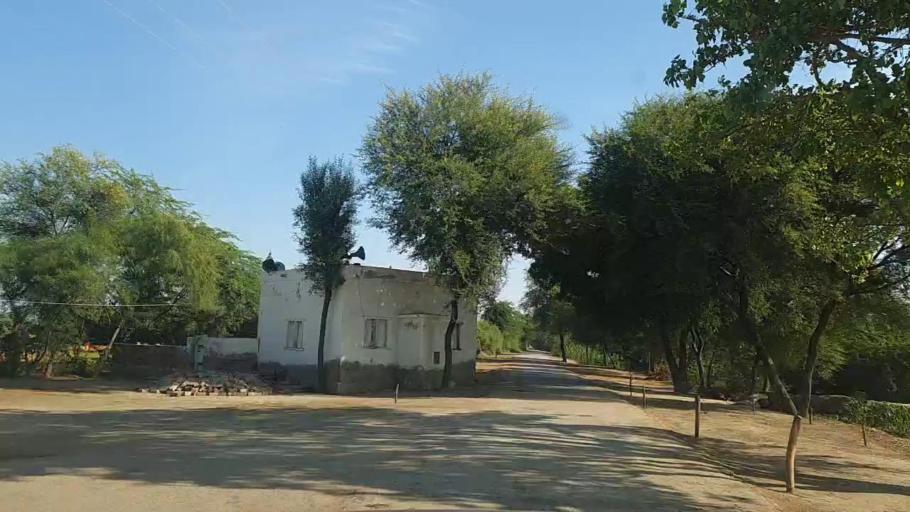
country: PK
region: Sindh
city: Bulri
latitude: 24.7934
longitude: 68.3424
